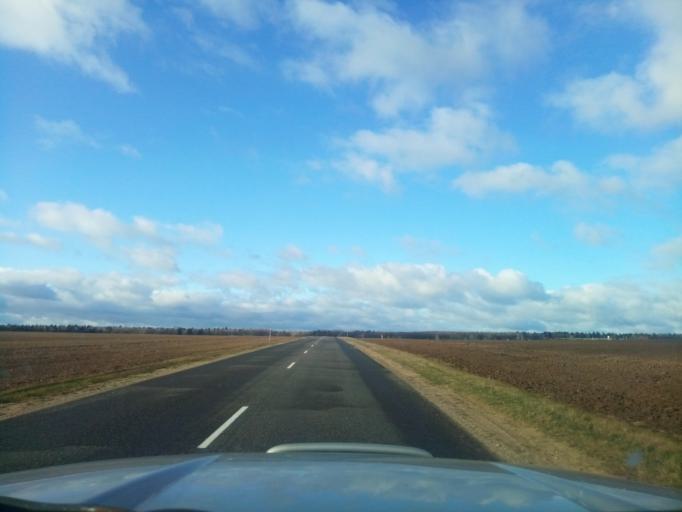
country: BY
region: Minsk
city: Kapyl'
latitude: 53.1697
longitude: 27.0461
